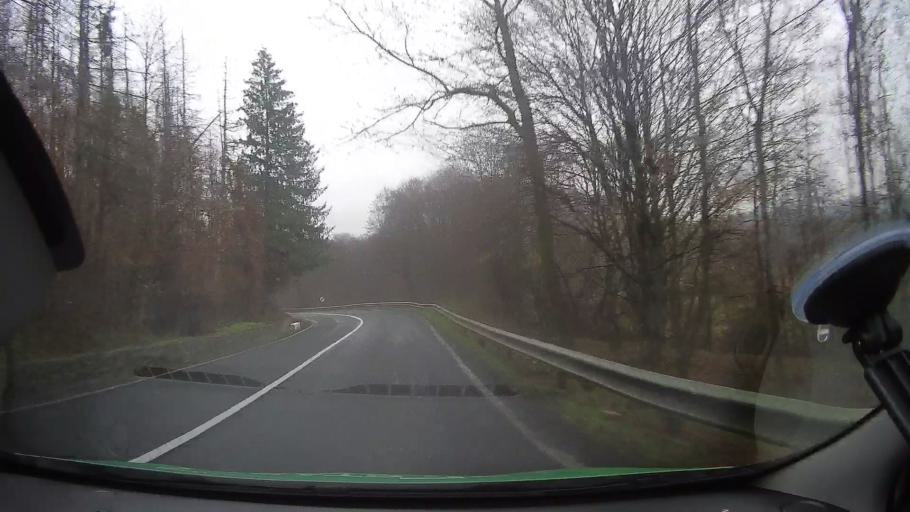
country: RO
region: Arad
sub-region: Comuna Plescuta
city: Plescuta
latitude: 46.2951
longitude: 22.4418
